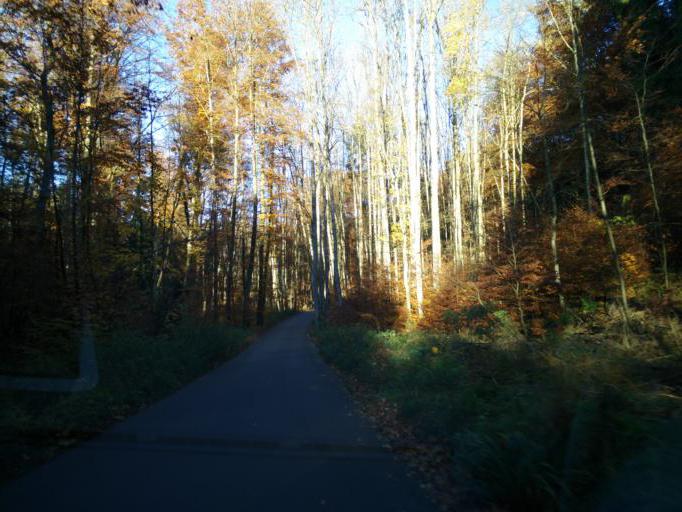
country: DE
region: Baden-Wuerttemberg
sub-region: Tuebingen Region
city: Gomaringen
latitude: 48.4278
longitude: 9.1079
